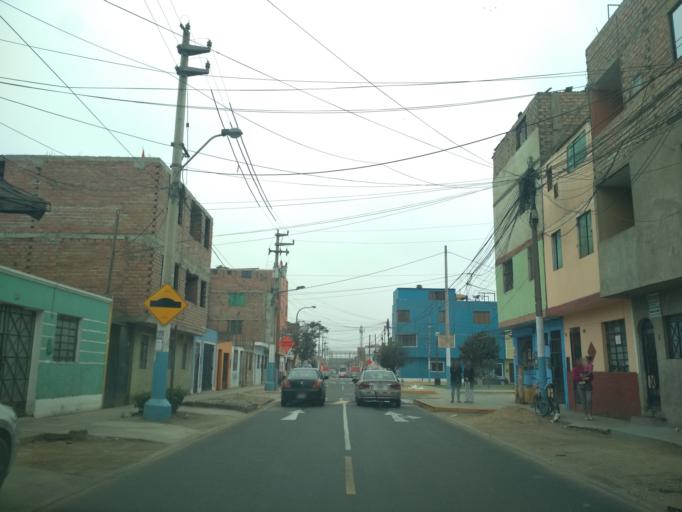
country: PE
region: Callao
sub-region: Callao
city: Callao
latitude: -12.0529
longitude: -77.1040
